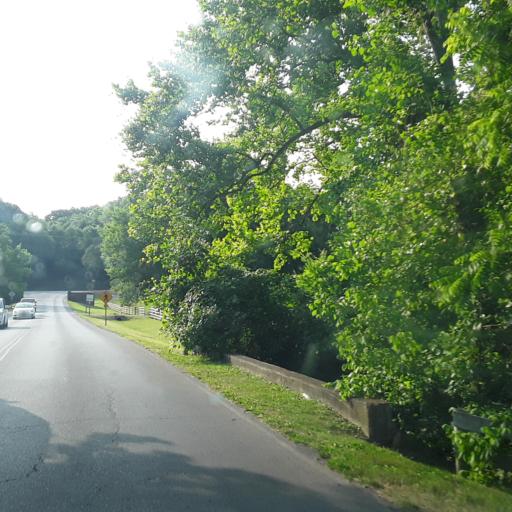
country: US
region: Tennessee
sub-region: Davidson County
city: Oak Hill
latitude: 36.0623
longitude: -86.7423
